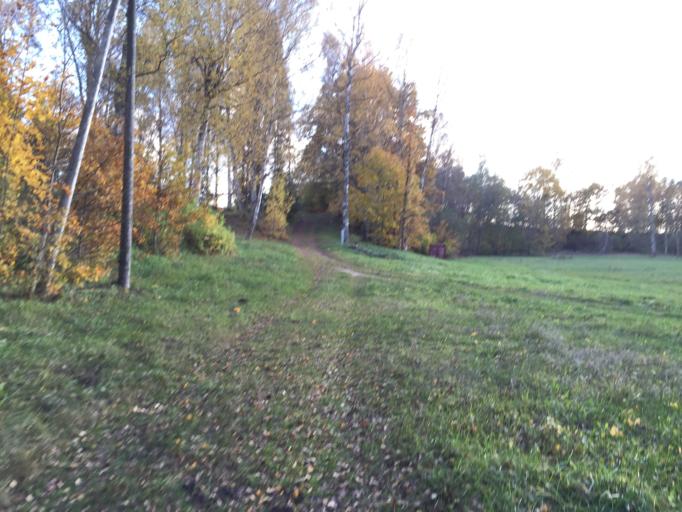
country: LV
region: Ogre
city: Jumprava
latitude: 56.7786
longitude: 25.0071
